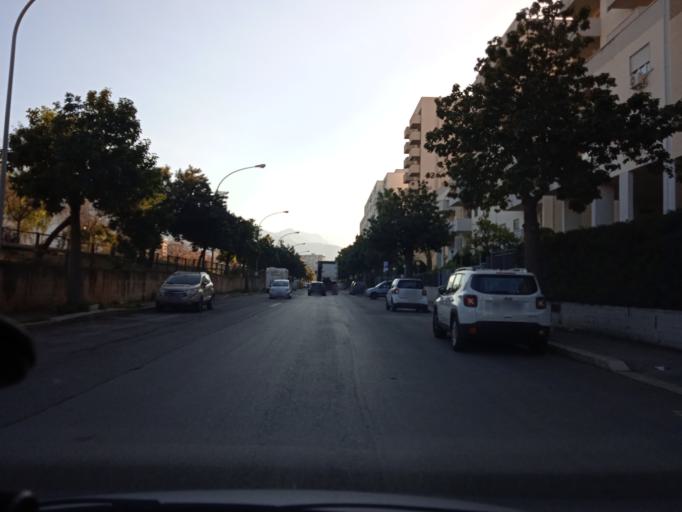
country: IT
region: Sicily
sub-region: Palermo
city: Ciaculli
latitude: 38.1076
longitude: 13.3773
